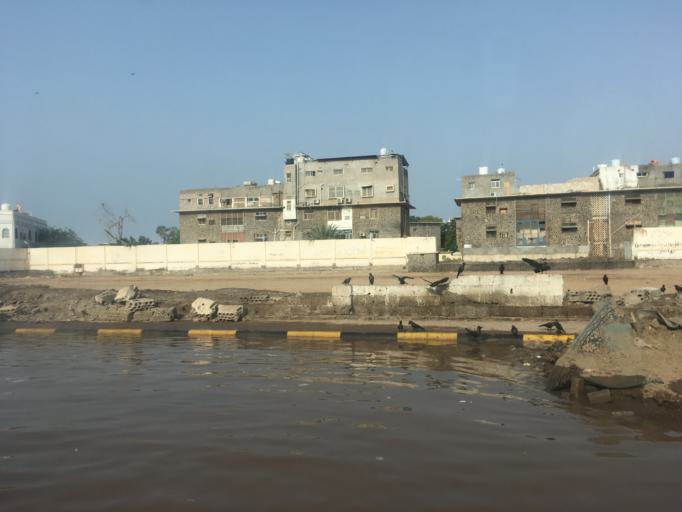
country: YE
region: Aden
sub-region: Attawahi
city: At Tawahi
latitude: 12.7792
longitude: 44.9798
